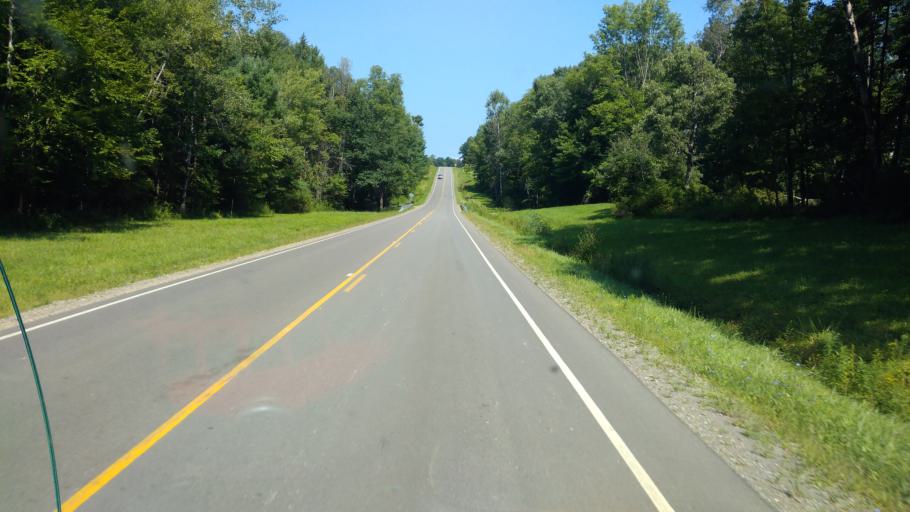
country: US
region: New York
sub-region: Allegany County
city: Belmont
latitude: 42.2660
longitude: -78.0421
